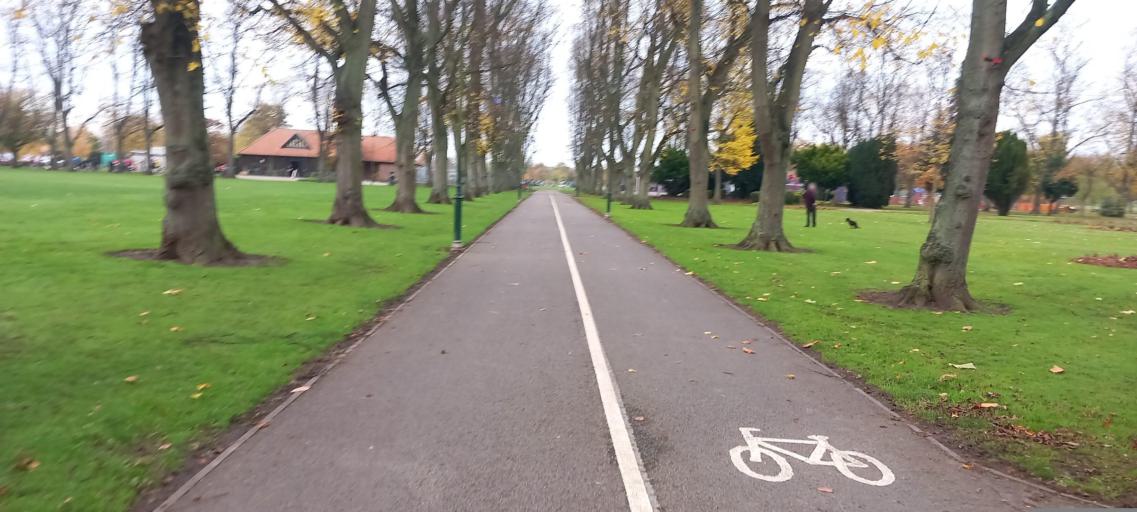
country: GB
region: England
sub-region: East Riding of Yorkshire
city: Airmyn
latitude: 53.7112
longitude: -0.8893
